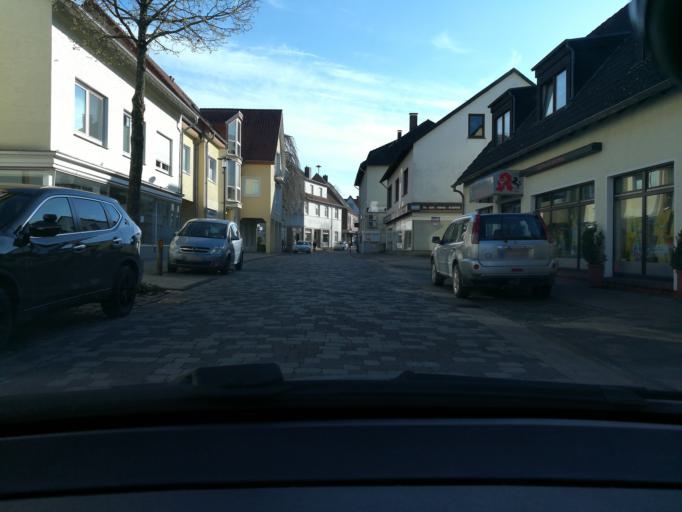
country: DE
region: North Rhine-Westphalia
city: Borgholzhausen
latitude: 52.1043
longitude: 8.3025
